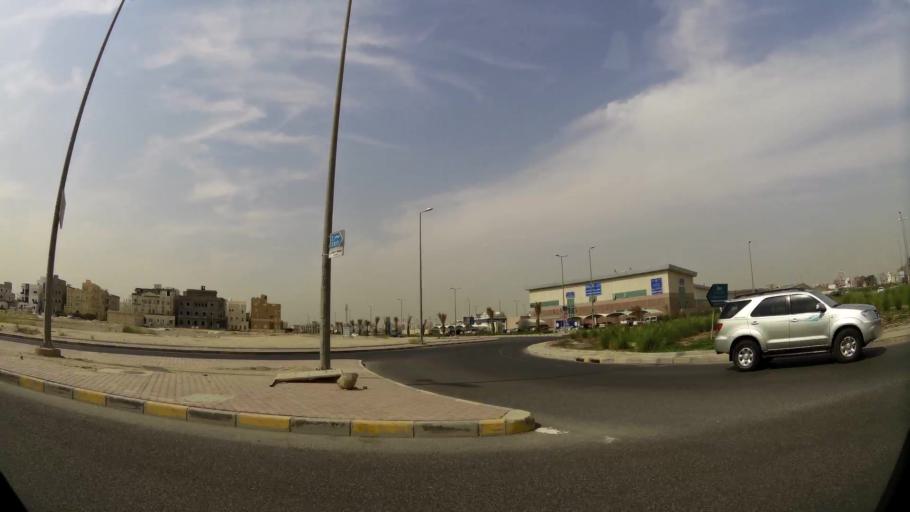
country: KW
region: Al Farwaniyah
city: Janub as Surrah
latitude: 29.2896
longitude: 47.9930
